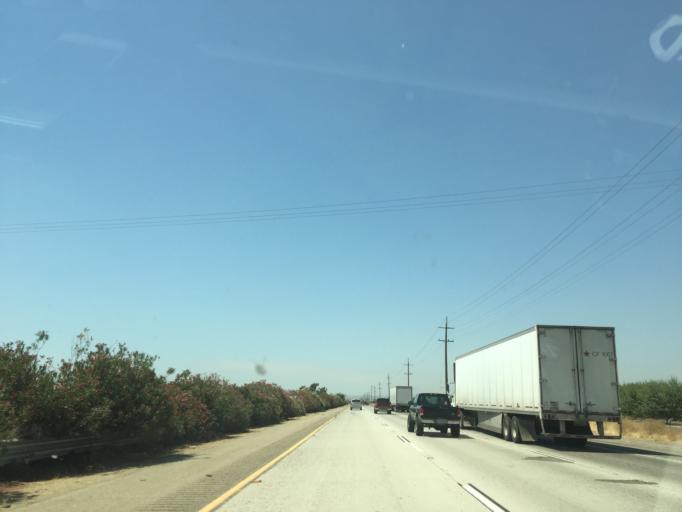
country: US
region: California
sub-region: Kern County
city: Weedpatch
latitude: 35.0337
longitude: -118.9601
